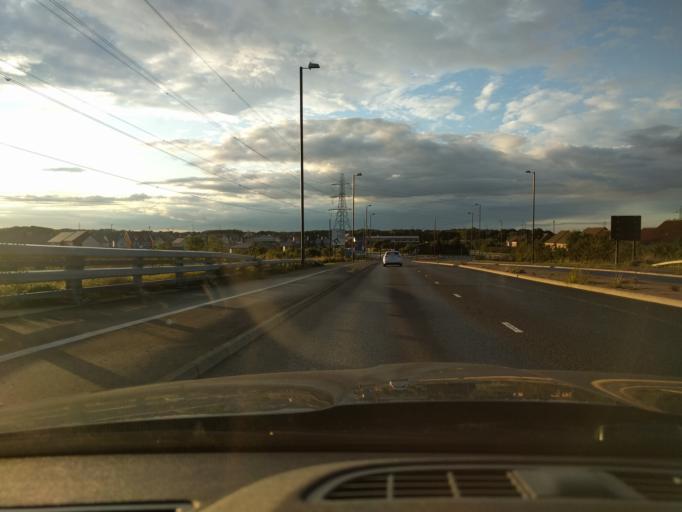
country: GB
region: England
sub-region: Northumberland
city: Backworth
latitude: 55.0327
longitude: -1.5216
